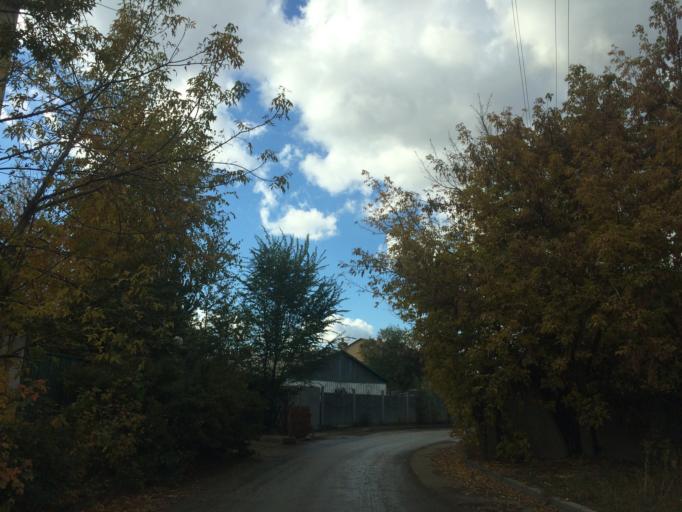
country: KZ
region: Astana Qalasy
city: Astana
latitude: 51.1855
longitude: 71.3687
